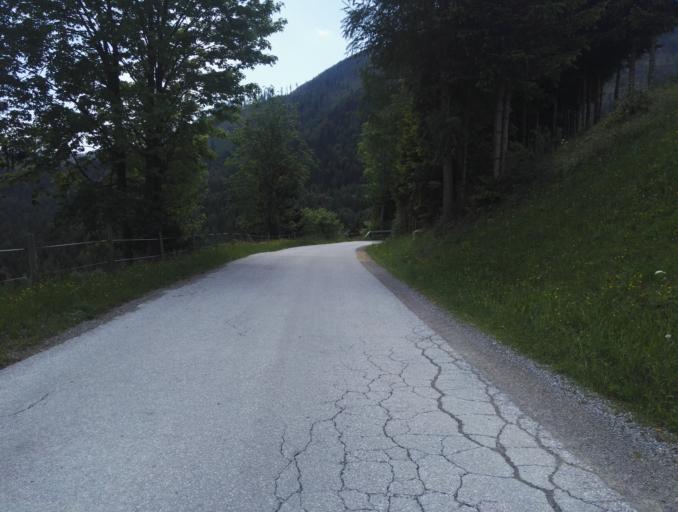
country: AT
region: Styria
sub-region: Politischer Bezirk Graz-Umgebung
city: Sankt Radegund bei Graz
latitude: 47.2128
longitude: 15.4579
